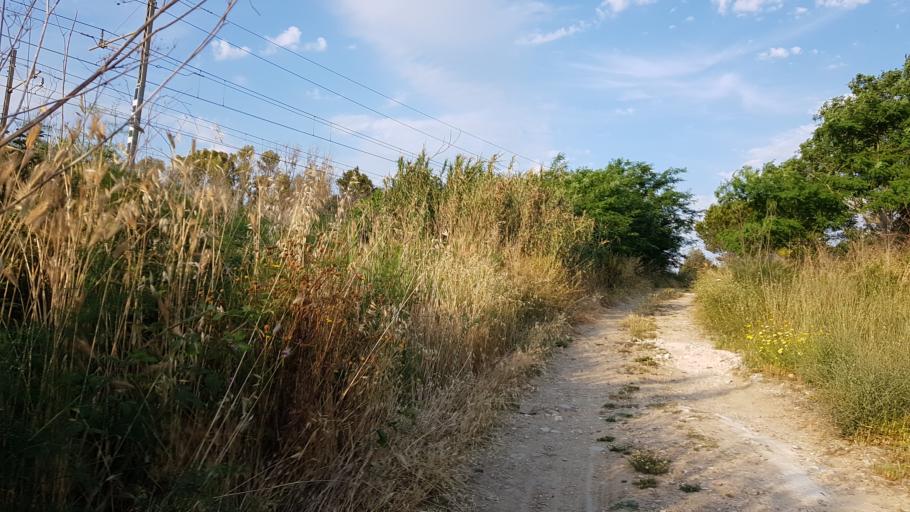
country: IT
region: Apulia
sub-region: Provincia di Brindisi
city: Brindisi
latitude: 40.6241
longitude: 17.8941
